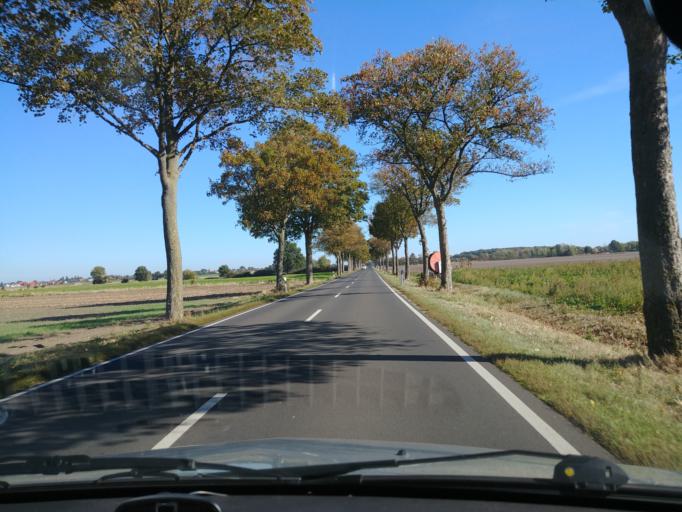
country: DE
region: Lower Saxony
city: Hillerse
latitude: 52.4202
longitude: 10.4176
